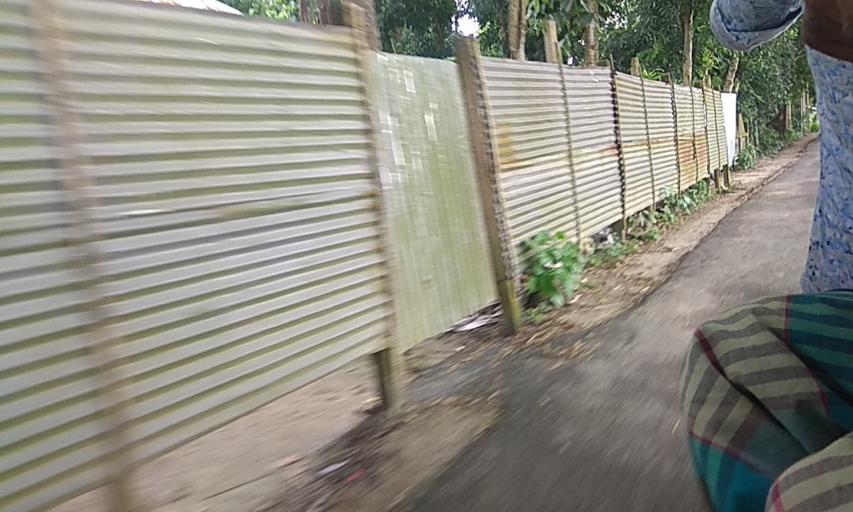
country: BD
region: Dhaka
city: Dohar
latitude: 23.4754
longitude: 90.0525
